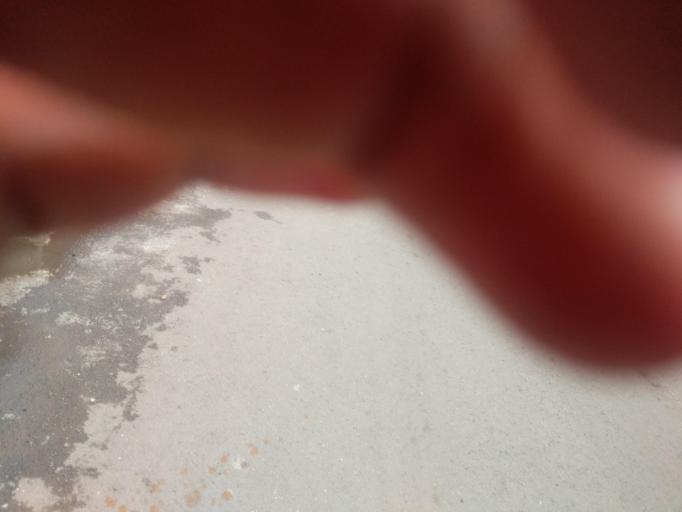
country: IN
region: Maharashtra
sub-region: Raigarh
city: Uran
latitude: 18.9494
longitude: 72.8250
